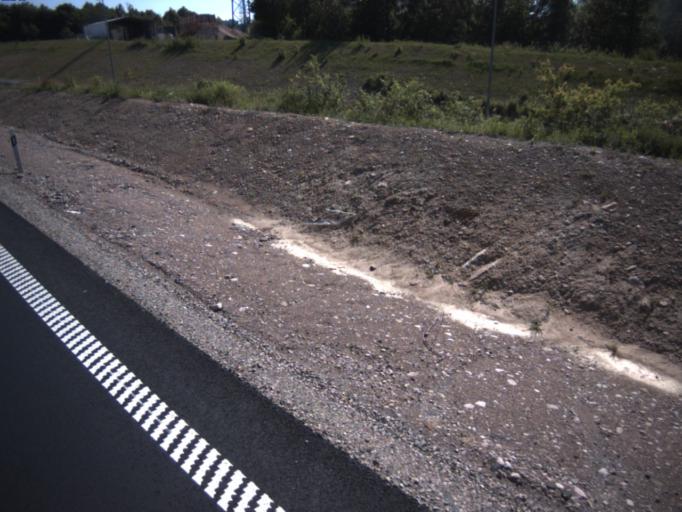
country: SE
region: Skane
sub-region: Helsingborg
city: Odakra
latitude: 56.0729
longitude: 12.7400
